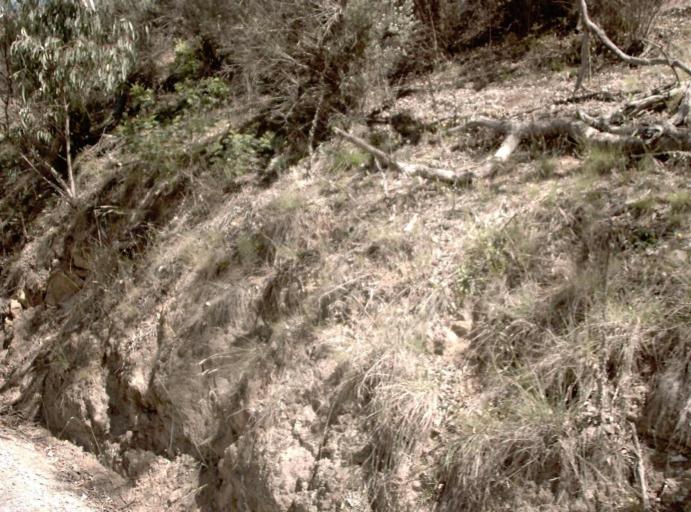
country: AU
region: New South Wales
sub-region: Snowy River
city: Jindabyne
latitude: -37.0455
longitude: 148.5602
